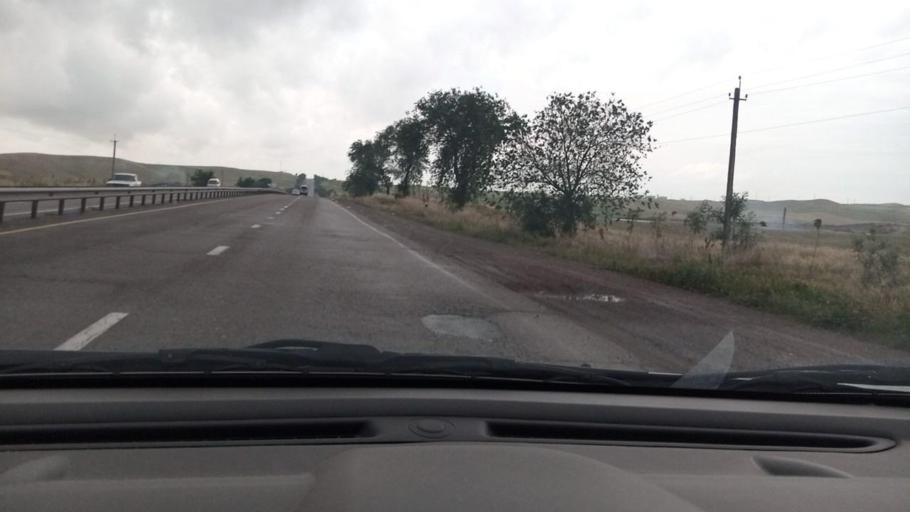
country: UZ
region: Toshkent
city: Ohangaron
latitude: 40.9478
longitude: 69.5738
